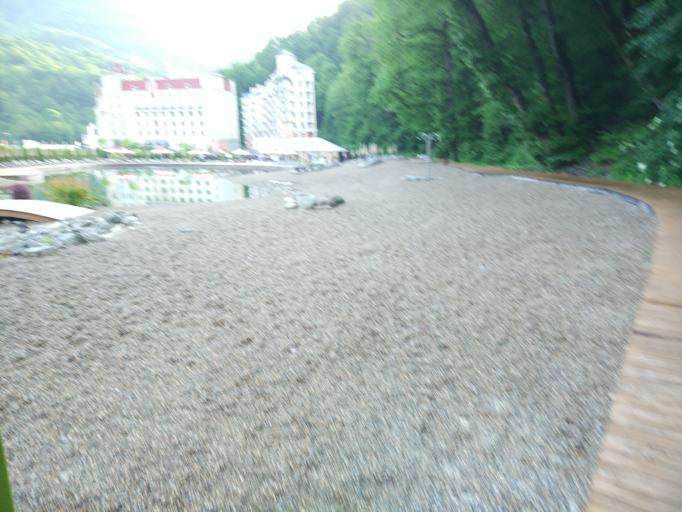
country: RU
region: Krasnodarskiy
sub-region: Sochi City
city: Krasnaya Polyana
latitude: 43.6739
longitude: 40.3002
